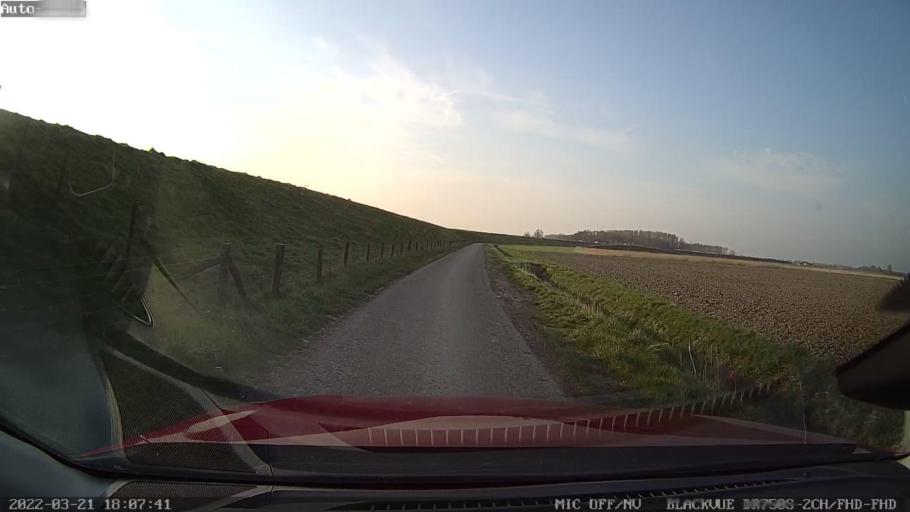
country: NL
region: Zeeland
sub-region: Gemeente Tholen
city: Tholen
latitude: 51.5583
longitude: 4.2366
